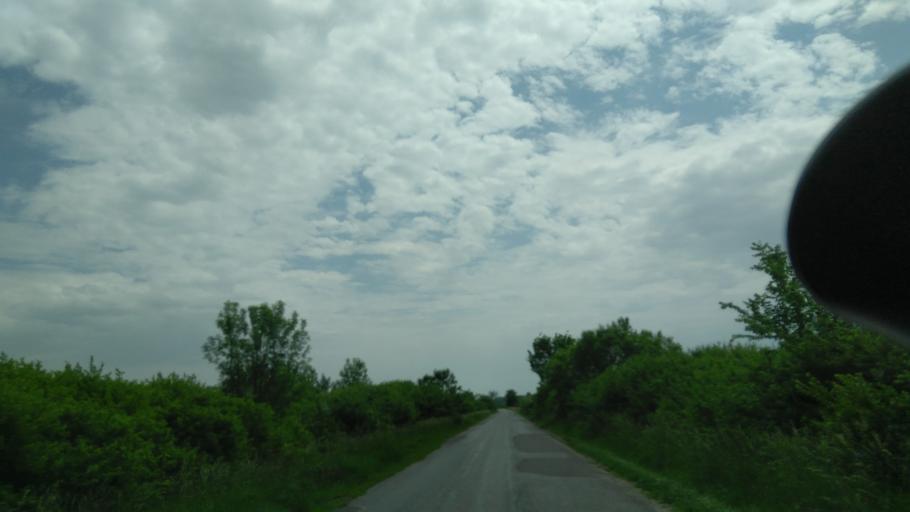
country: RO
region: Bihor
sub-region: Comuna Sannicolau-Roman
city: Sannicolau Roman
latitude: 47.0060
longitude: 21.6127
